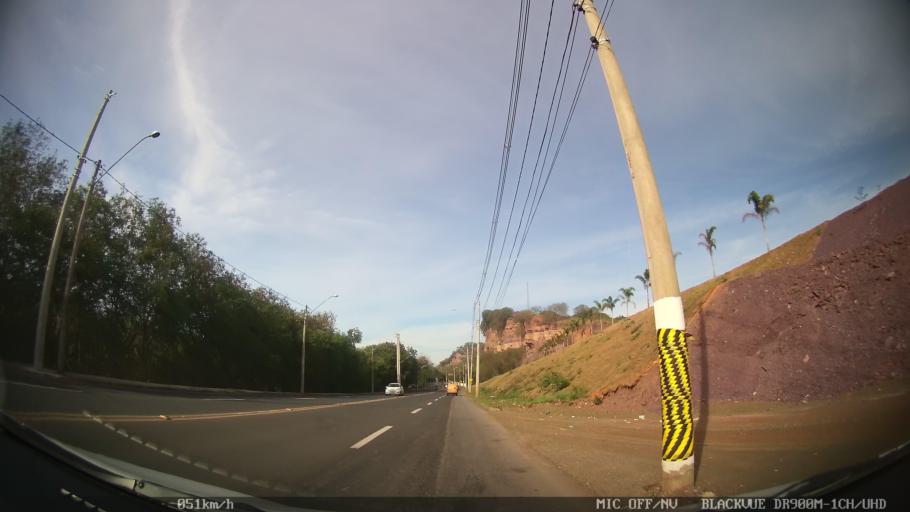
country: BR
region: Sao Paulo
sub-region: Piracicaba
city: Piracicaba
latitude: -22.7108
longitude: -47.6772
